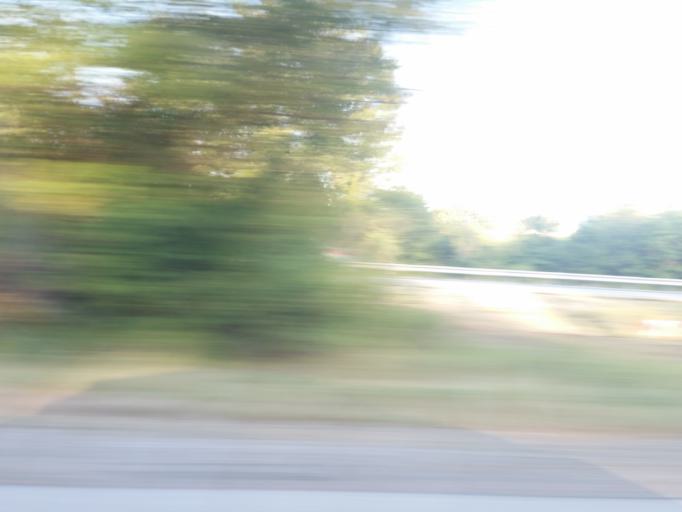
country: US
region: Indiana
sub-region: Boone County
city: Lebanon
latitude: 40.0597
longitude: -86.4941
